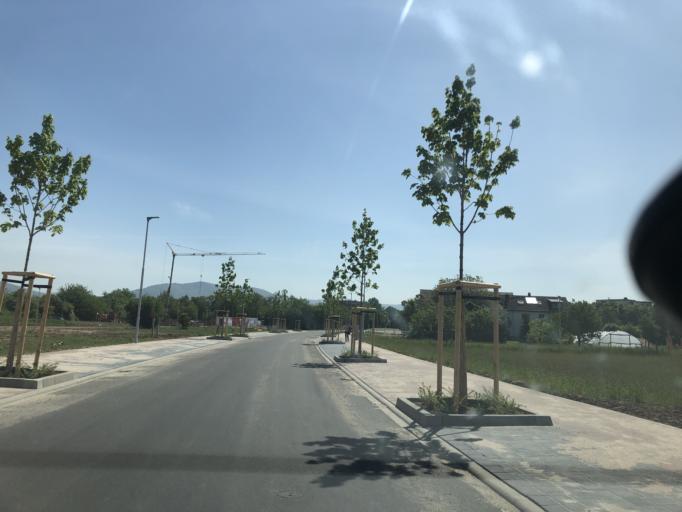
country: DE
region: Baden-Wuerttemberg
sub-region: Karlsruhe Region
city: Ladenburg
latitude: 49.4778
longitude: 8.6150
